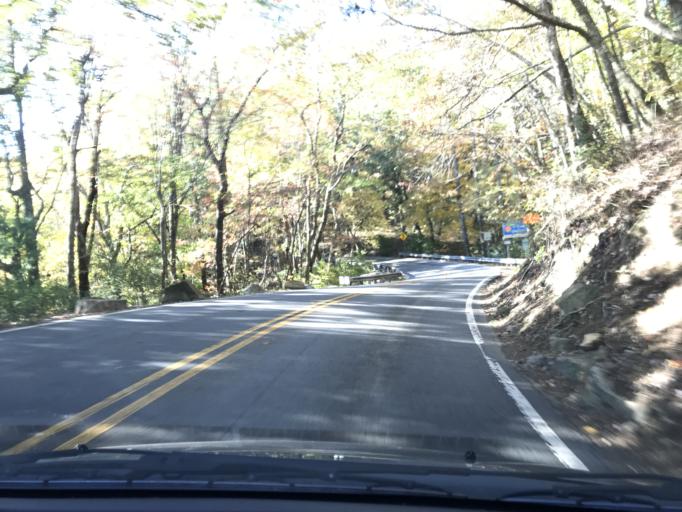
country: US
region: Tennessee
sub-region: Hamilton County
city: Lookout Mountain
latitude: 34.9832
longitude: -85.3447
